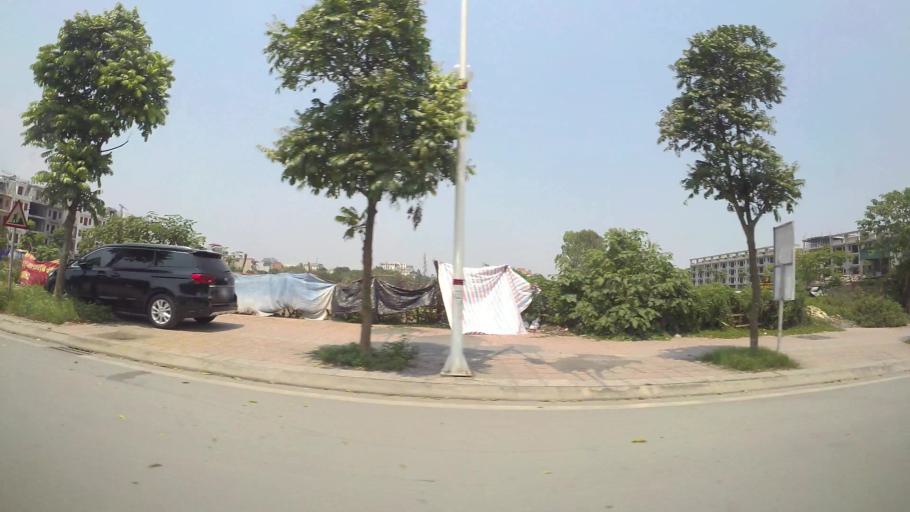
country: VN
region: Ha Noi
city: Hoan Kiem
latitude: 21.0374
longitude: 105.8777
